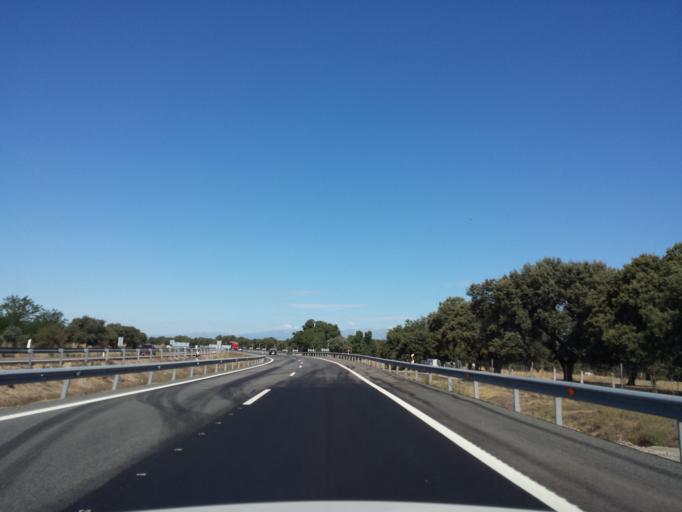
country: ES
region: Castille-La Mancha
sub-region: Province of Toledo
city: Alcanizo
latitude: 39.9215
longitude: -5.0855
